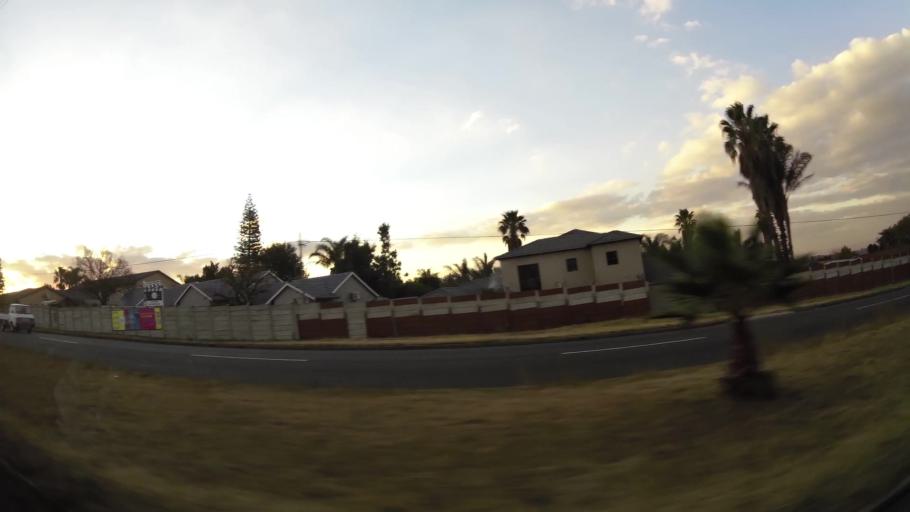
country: ZA
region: Gauteng
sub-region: West Rand District Municipality
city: Krugersdorp
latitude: -26.0760
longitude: 27.7851
